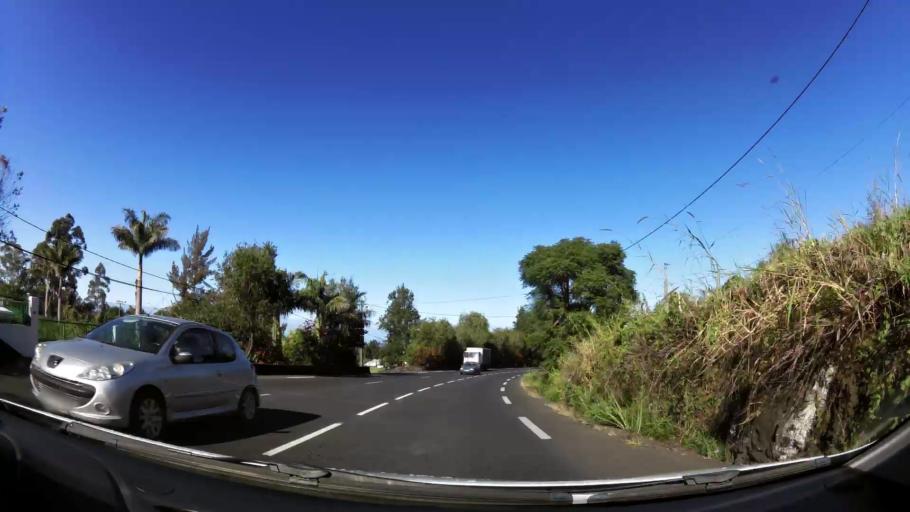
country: RE
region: Reunion
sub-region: Reunion
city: Le Tampon
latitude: -21.2392
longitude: 55.5298
